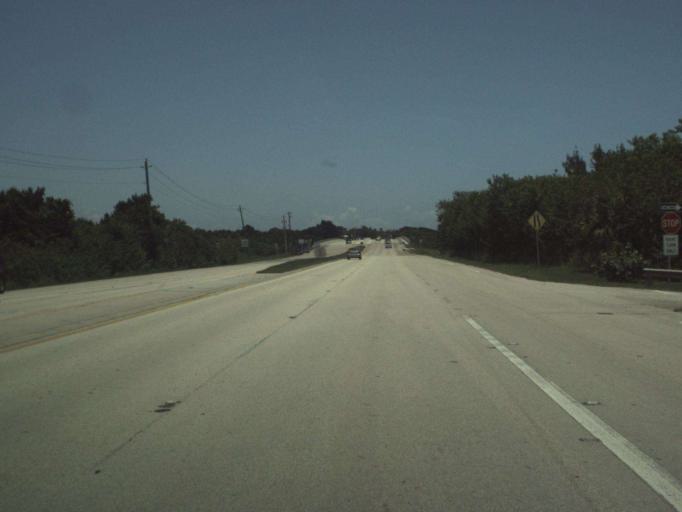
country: US
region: Florida
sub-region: Indian River County
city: Roseland
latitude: 27.8505
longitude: -80.4898
